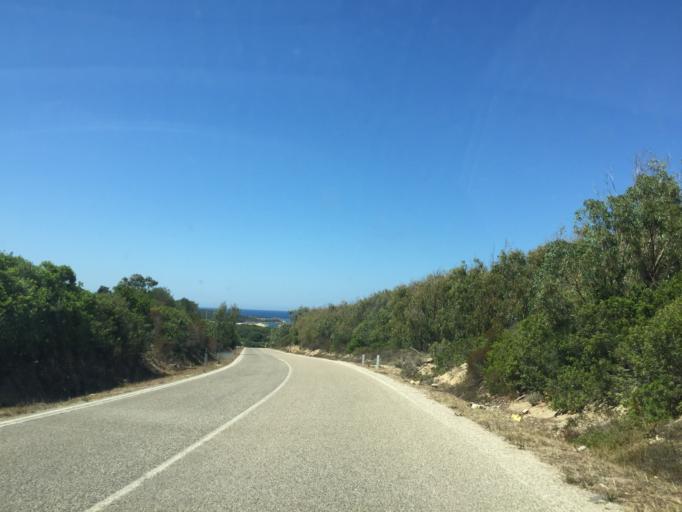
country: IT
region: Sardinia
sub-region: Provincia di Olbia-Tempio
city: Aglientu
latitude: 41.1188
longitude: 9.0731
